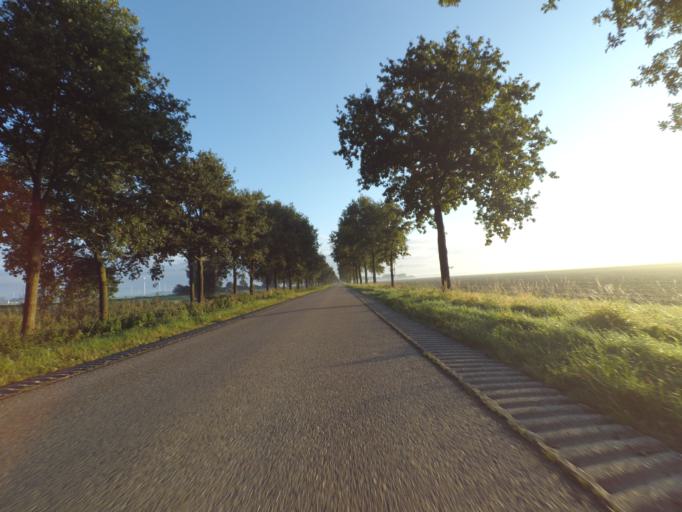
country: NL
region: Flevoland
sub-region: Gemeente Zeewolde
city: Zeewolde
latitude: 52.3707
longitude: 5.5174
